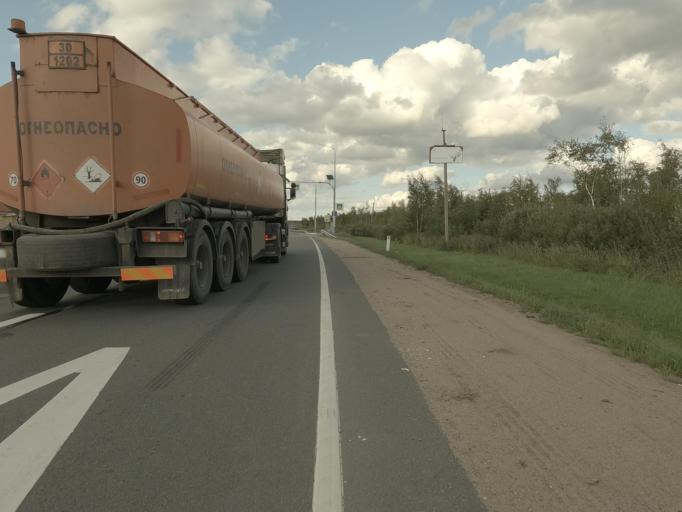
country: RU
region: Leningrad
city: Mga
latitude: 59.7460
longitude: 31.0852
